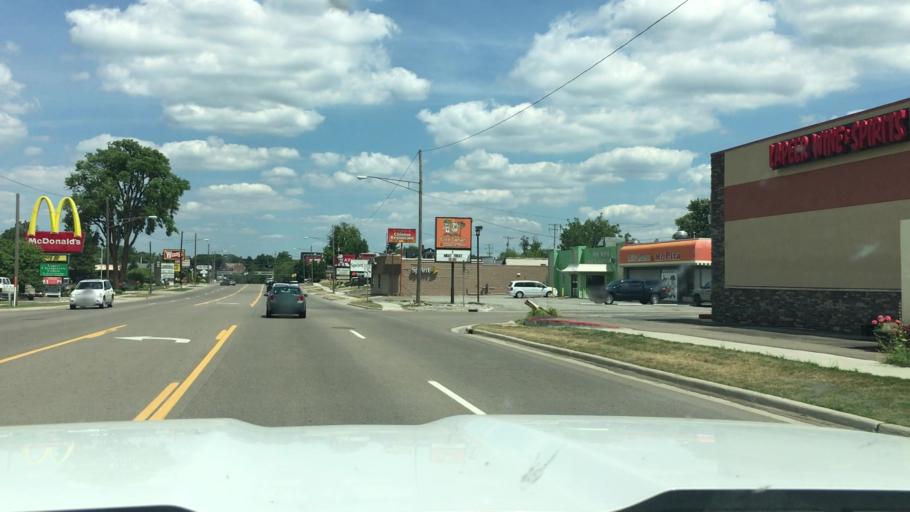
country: US
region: Michigan
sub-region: Lapeer County
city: Lapeer
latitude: 43.0447
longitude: -83.3196
